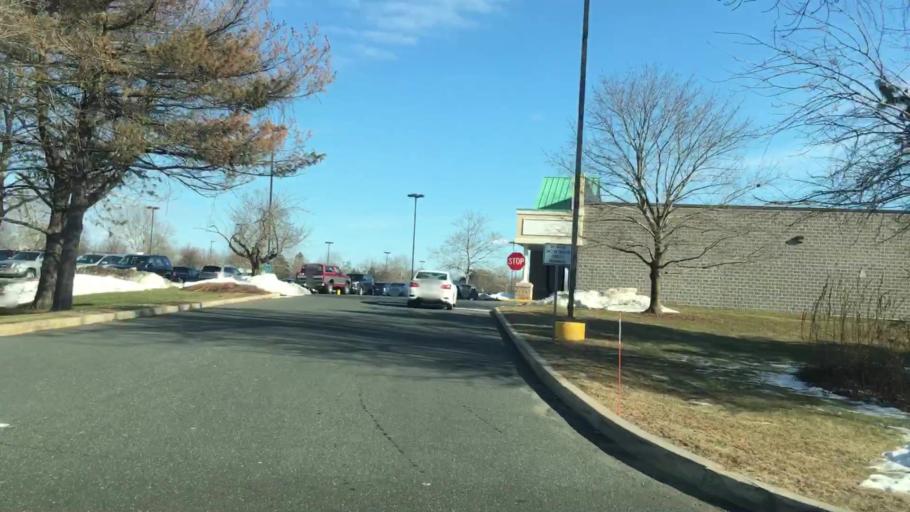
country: US
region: Connecticut
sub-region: Hartford County
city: Enfield
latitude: 41.9882
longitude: -72.5835
